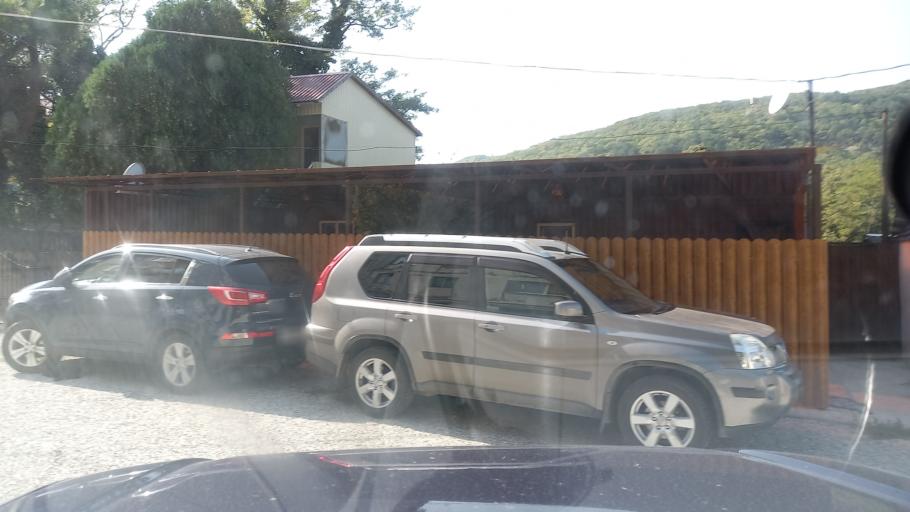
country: RU
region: Krasnodarskiy
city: Pshada
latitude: 44.3770
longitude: 38.4018
